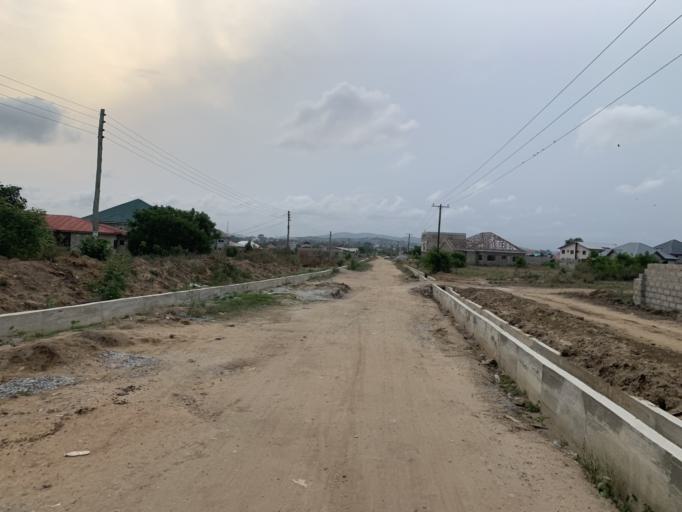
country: GH
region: Central
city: Winneba
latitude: 5.3829
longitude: -0.6273
